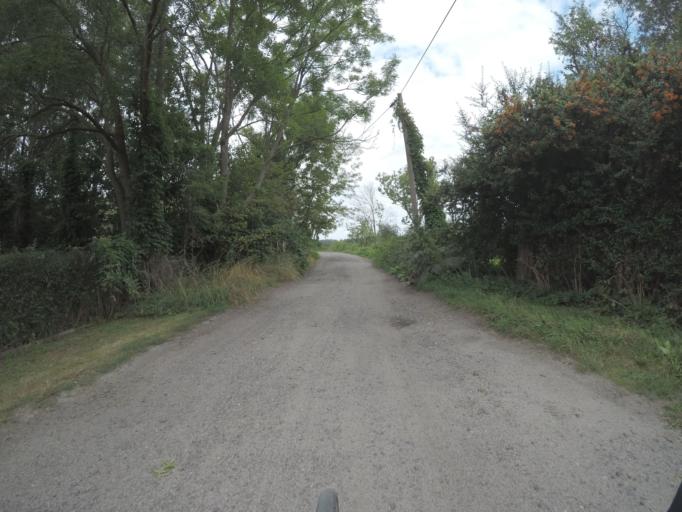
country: DE
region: Brandenburg
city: Nauen
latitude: 52.6123
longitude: 12.9231
